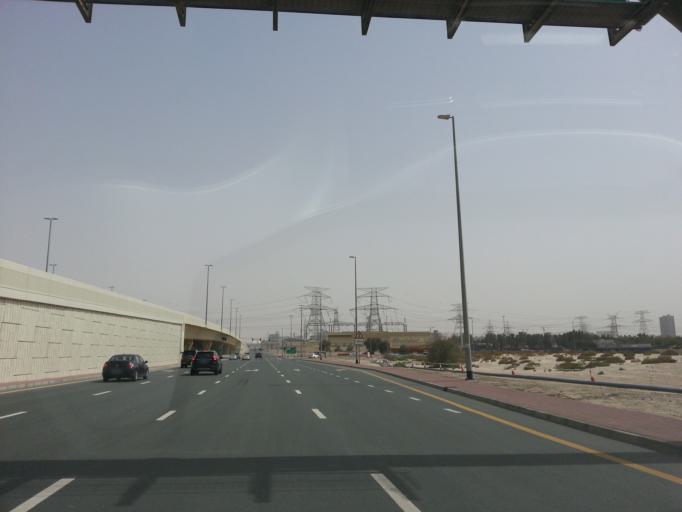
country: AE
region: Dubai
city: Dubai
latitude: 25.0694
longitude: 55.1909
